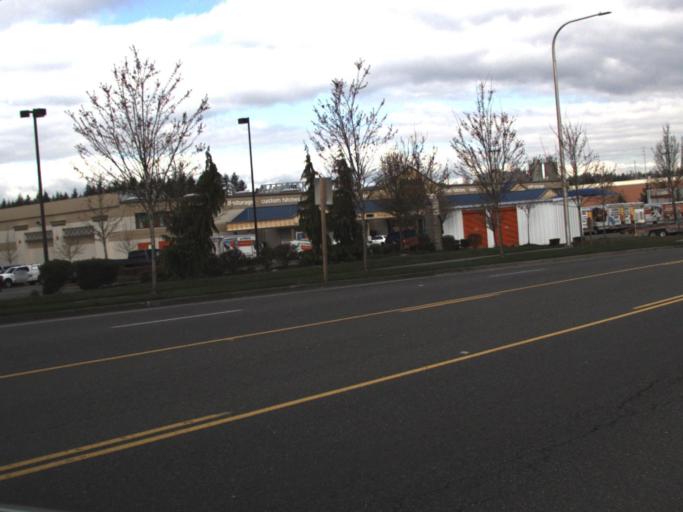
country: US
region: Washington
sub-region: King County
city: Lakeland South
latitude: 47.2844
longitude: -122.3136
